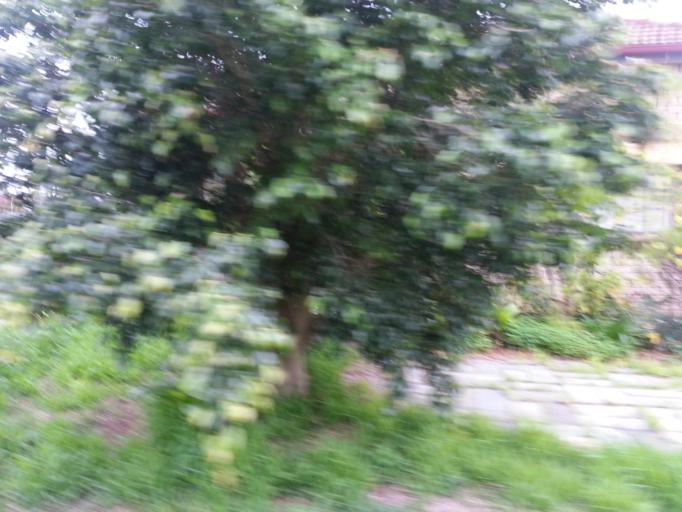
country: AU
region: South Australia
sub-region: Port Adelaide Enfield
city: Alberton
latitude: -34.8496
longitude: 138.5215
